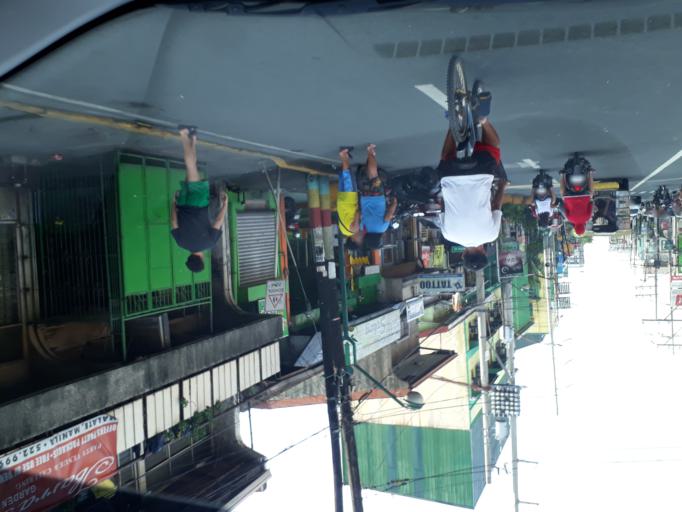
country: PH
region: Metro Manila
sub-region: City of Manila
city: Manila
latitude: 14.6301
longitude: 120.9742
